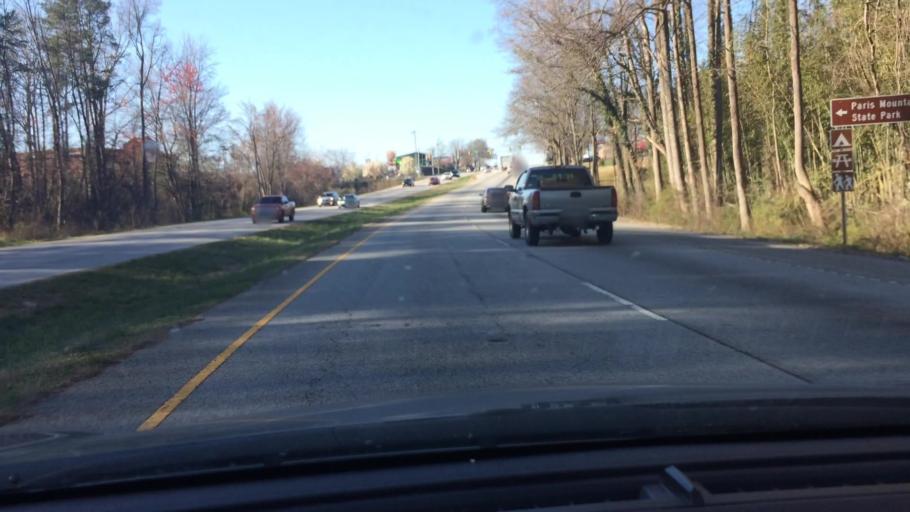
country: US
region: South Carolina
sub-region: Greenville County
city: Travelers Rest
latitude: 34.9660
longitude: -82.4301
